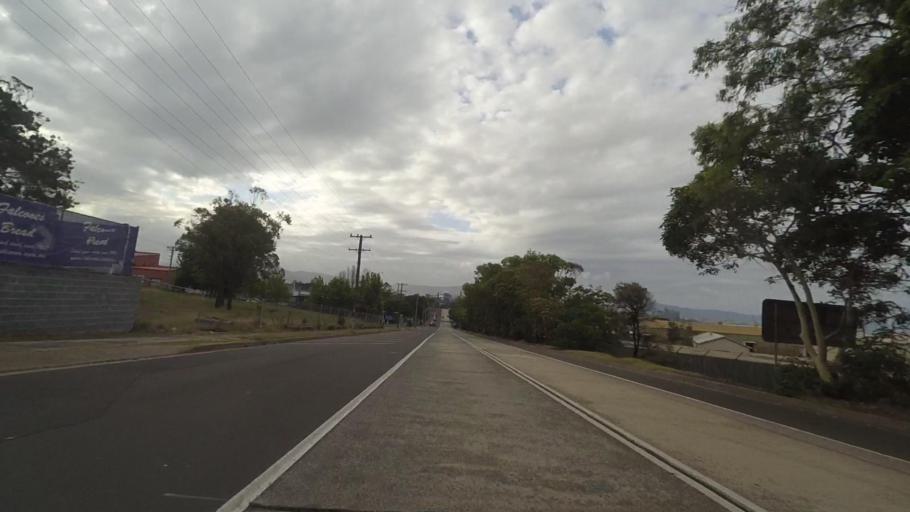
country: AU
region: New South Wales
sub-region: Wollongong
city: Port Kembla
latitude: -34.4827
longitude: 150.9049
